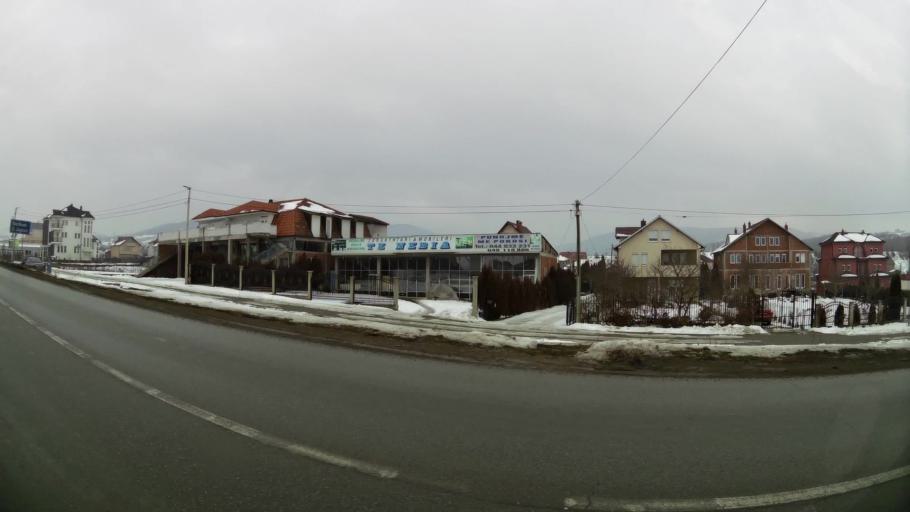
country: XK
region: Pristina
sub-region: Komuna e Prishtines
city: Pristina
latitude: 42.7090
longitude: 21.1533
